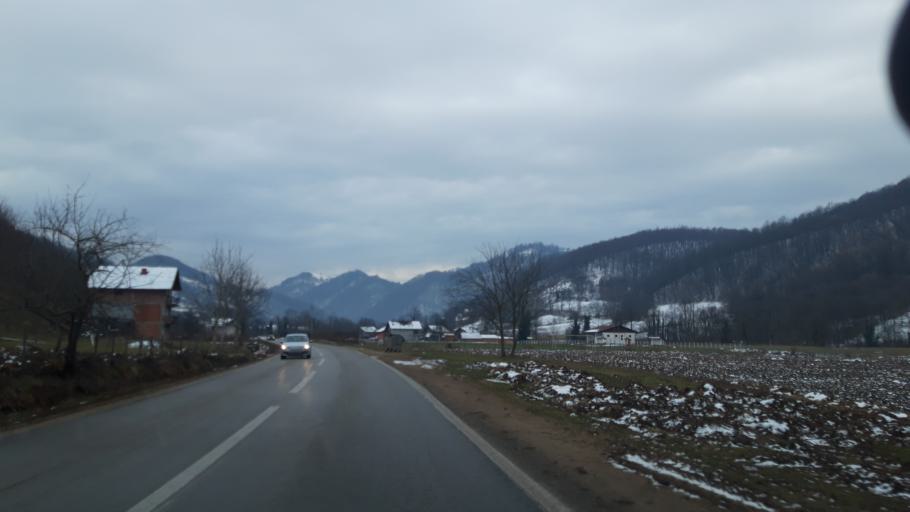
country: BA
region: Republika Srpska
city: Milici
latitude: 44.2215
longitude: 19.1004
